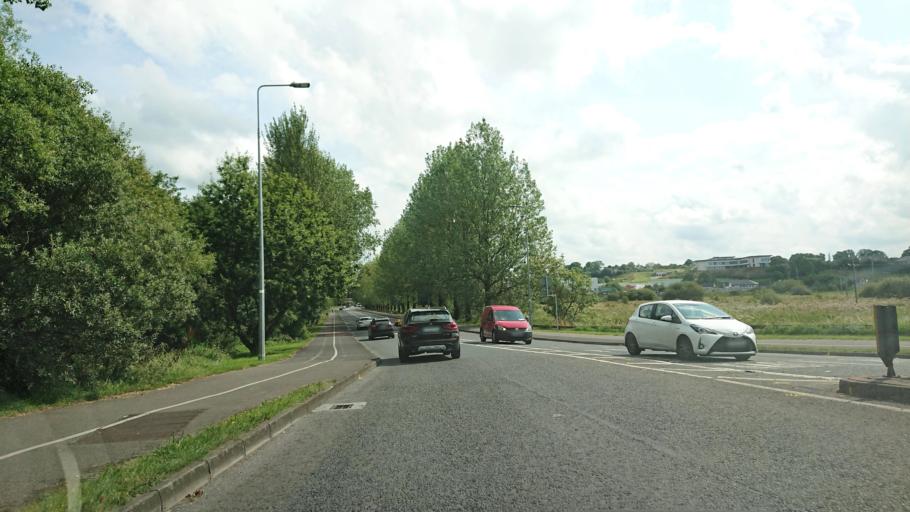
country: IE
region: Connaught
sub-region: County Leitrim
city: Carrick-on-Shannon
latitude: 53.9452
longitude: -8.0859
